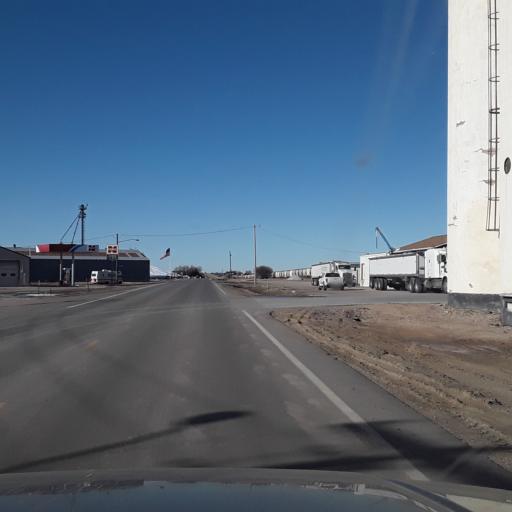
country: US
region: Nebraska
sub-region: Gosper County
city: Elwood
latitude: 40.5286
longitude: -99.6348
